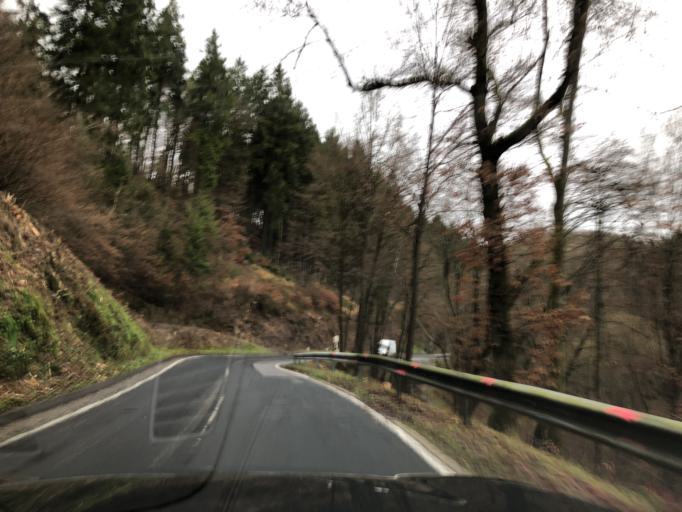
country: DE
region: Rheinland-Pfalz
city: Kasbach-Ohlenberg
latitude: 50.6100
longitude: 7.2819
